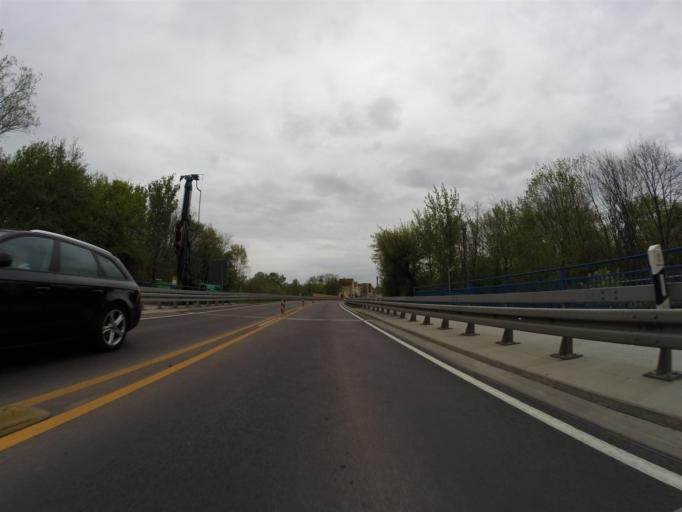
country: DE
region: Saxony-Anhalt
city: Schkopau
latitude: 51.4220
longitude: 11.9838
